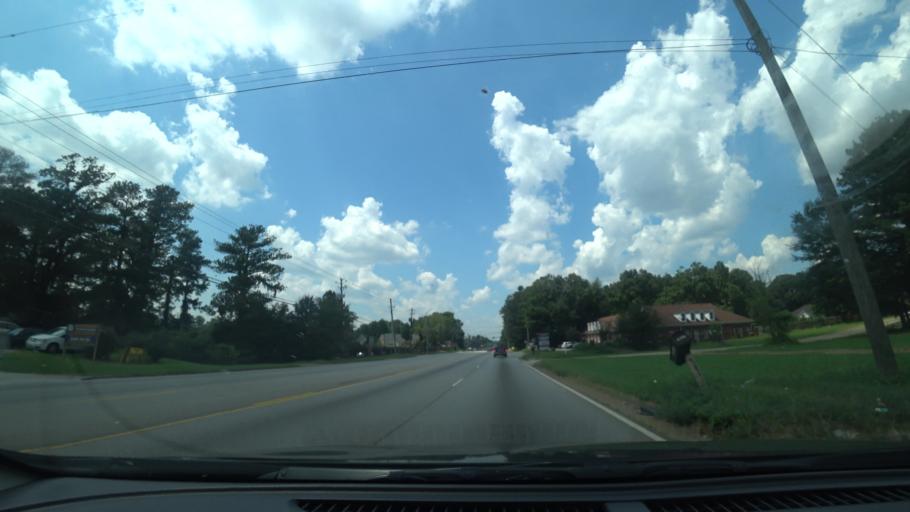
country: US
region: Georgia
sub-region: DeKalb County
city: Belvedere Park
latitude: 33.7467
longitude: -84.2203
